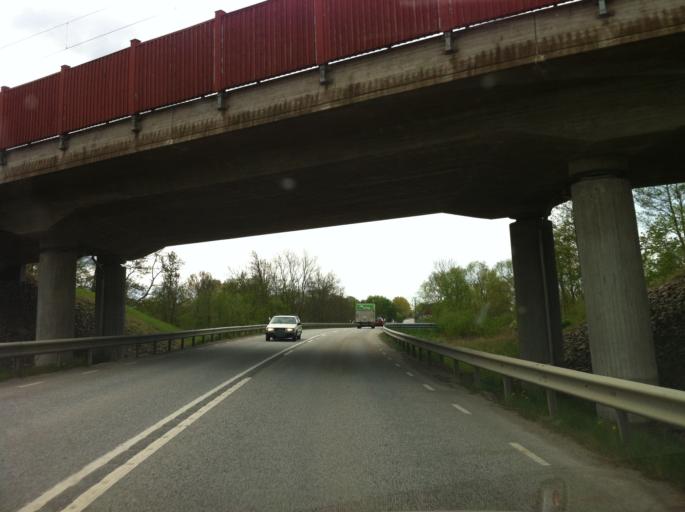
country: SE
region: Skane
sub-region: Landskrona
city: Asmundtorp
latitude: 55.8464
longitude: 12.9670
